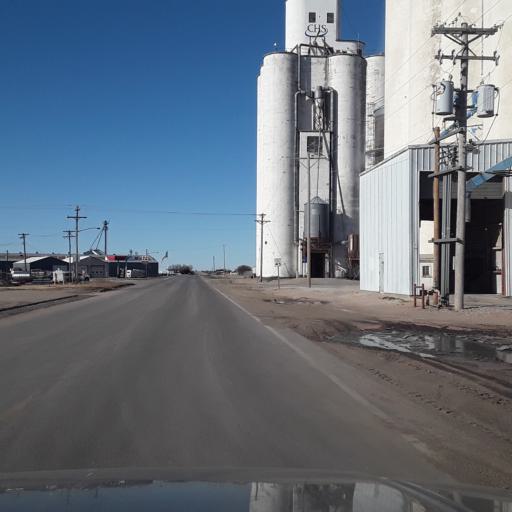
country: US
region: Nebraska
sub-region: Gosper County
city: Elwood
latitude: 40.5282
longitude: -99.6338
